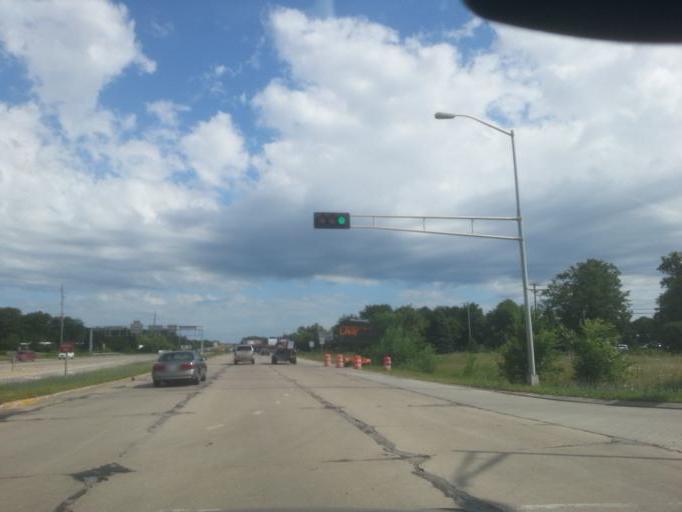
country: US
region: Wisconsin
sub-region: Dane County
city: Monona
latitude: 43.0482
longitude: -89.3077
